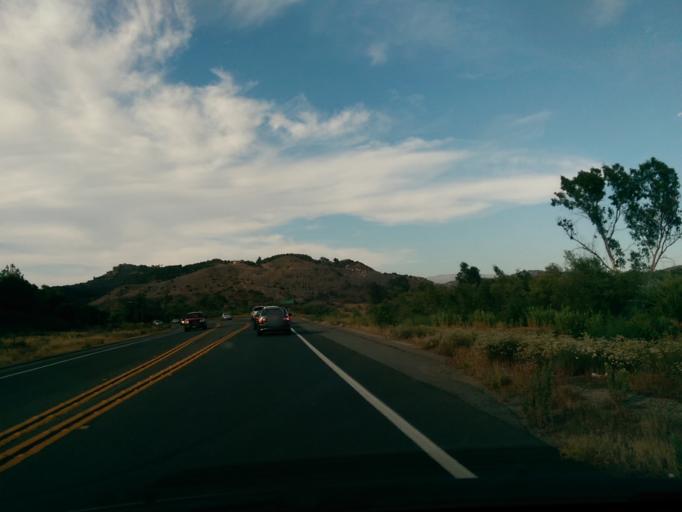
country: US
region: California
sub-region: San Diego County
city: Bonsall
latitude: 33.3123
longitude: -117.1996
